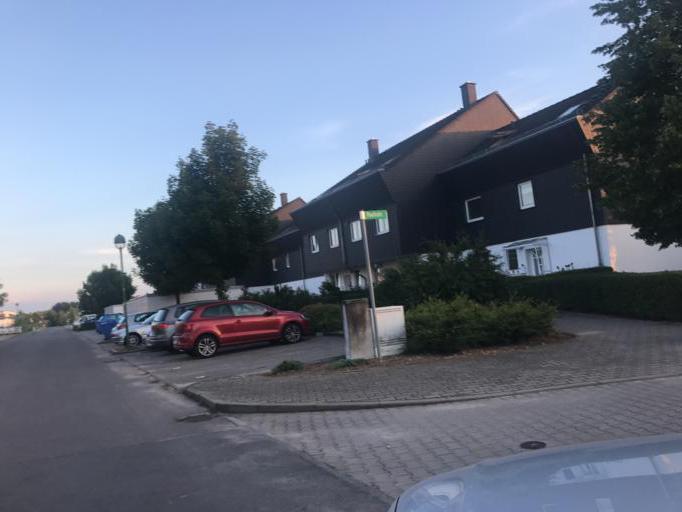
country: DE
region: Brandenburg
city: Melchow
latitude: 52.8516
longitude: 13.6947
